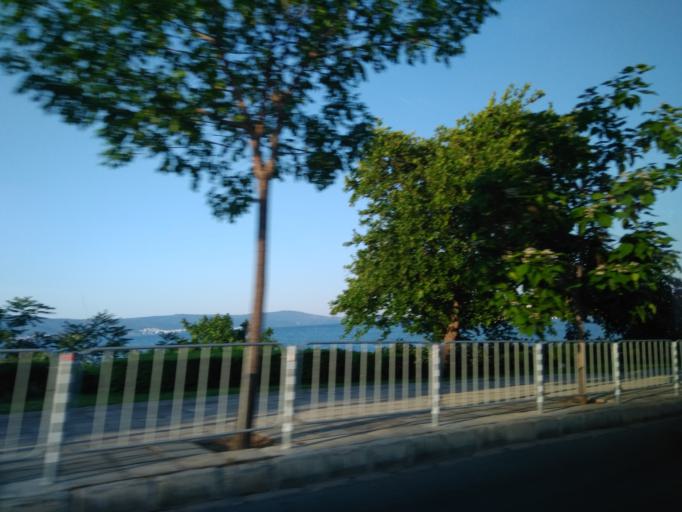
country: BG
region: Burgas
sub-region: Obshtina Nesebur
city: Nesebar
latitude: 42.6600
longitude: 27.7246
